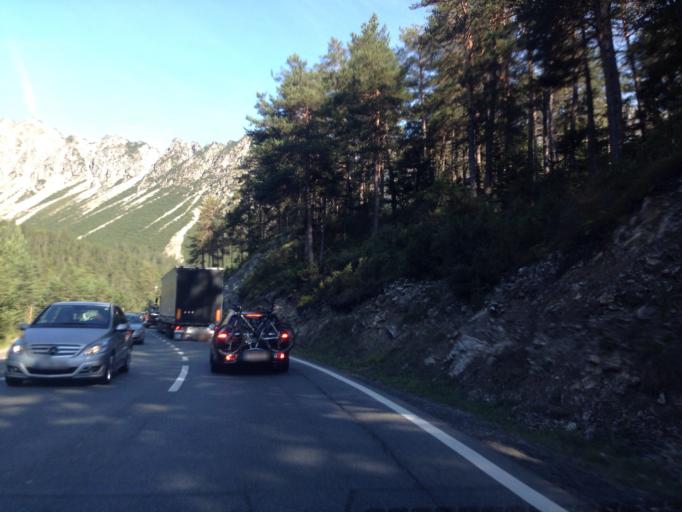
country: AT
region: Tyrol
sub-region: Politischer Bezirk Imst
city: Nassereith
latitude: 47.3577
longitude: 10.8245
